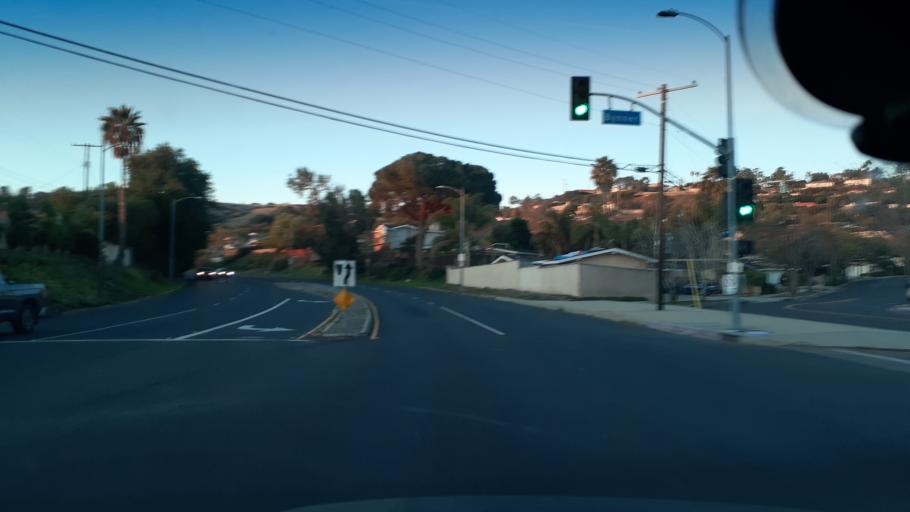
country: US
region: California
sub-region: Los Angeles County
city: San Pedro
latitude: 33.7385
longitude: -118.3151
